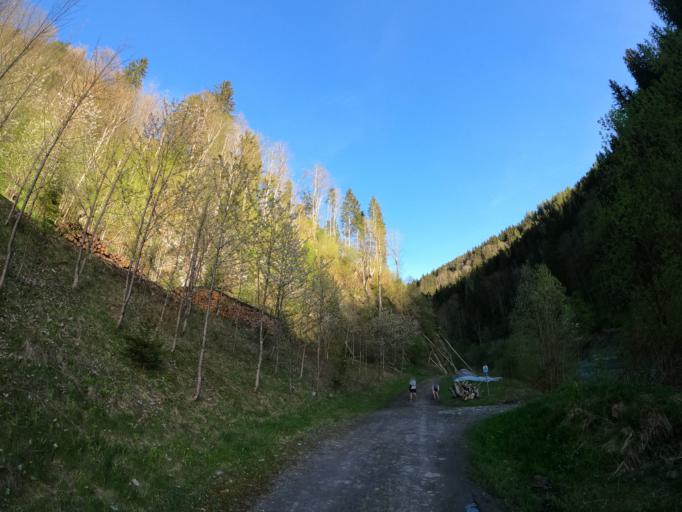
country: AT
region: Salzburg
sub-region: Politischer Bezirk Sankt Johann im Pongau
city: Sankt Johann im Pongau
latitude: 47.3346
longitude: 13.2168
